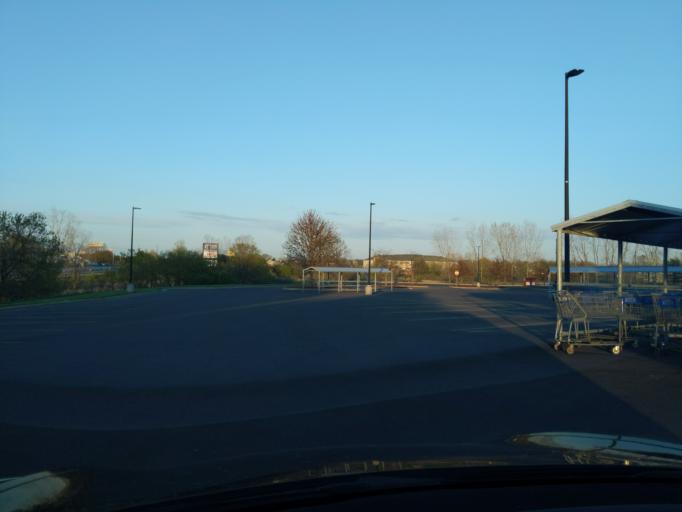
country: US
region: Michigan
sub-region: Jackson County
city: Jackson
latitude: 42.2684
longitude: -84.4608
